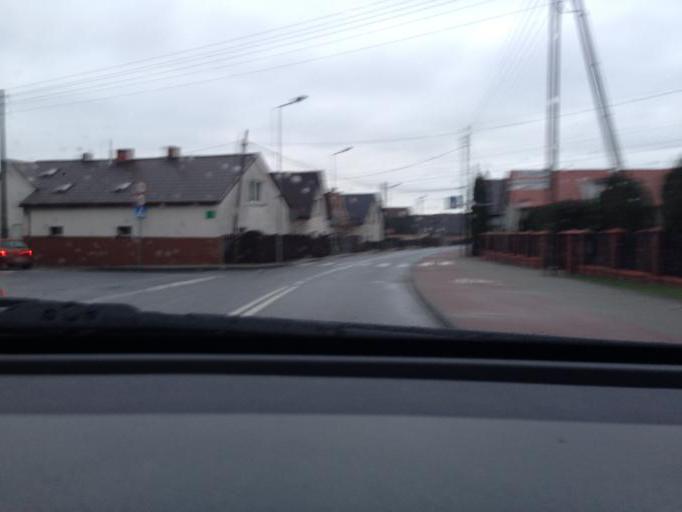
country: PL
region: Opole Voivodeship
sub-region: Powiat opolski
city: Opole
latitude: 50.6808
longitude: 17.9583
